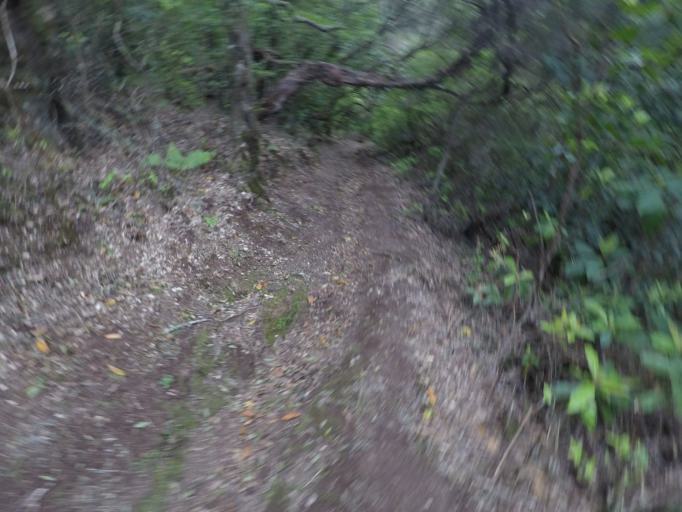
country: PT
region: Madeira
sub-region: Camara de Lobos
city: Curral das Freiras
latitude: 32.7718
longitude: -16.9780
